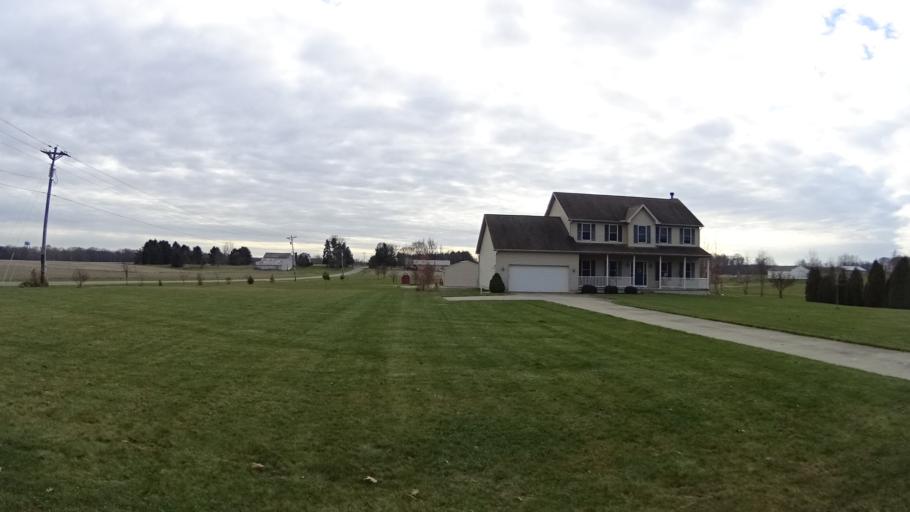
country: US
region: Ohio
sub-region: Lorain County
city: Camden
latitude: 41.2760
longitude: -82.3169
